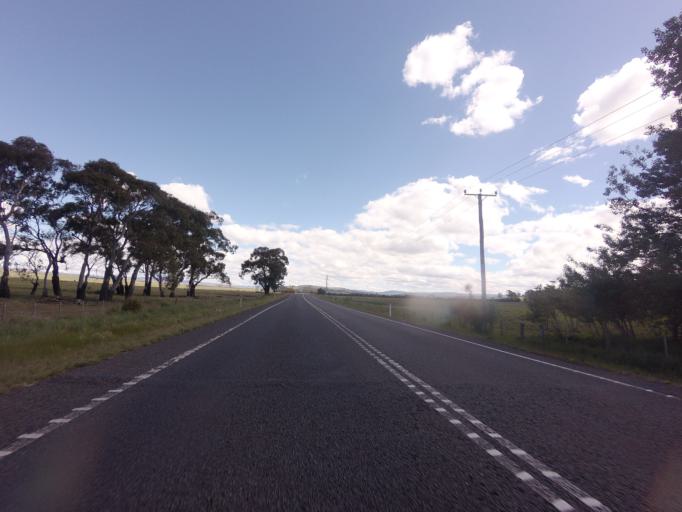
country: AU
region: Tasmania
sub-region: Northern Midlands
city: Evandale
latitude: -41.9899
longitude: 147.5055
